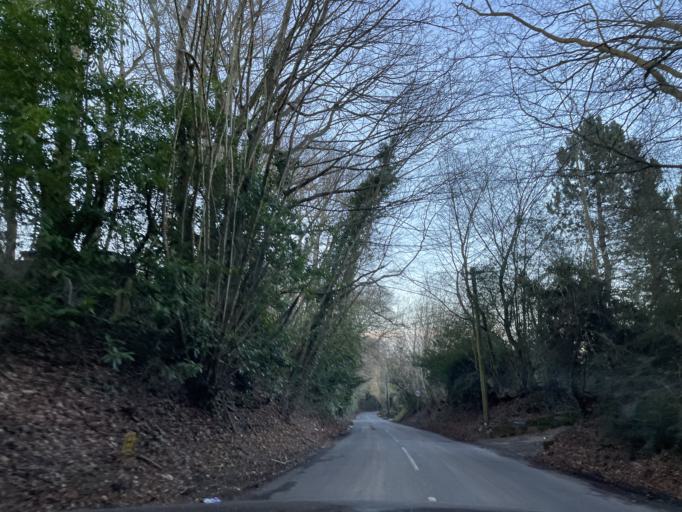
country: GB
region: England
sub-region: Kent
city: Westerham
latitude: 51.2692
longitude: 0.1265
